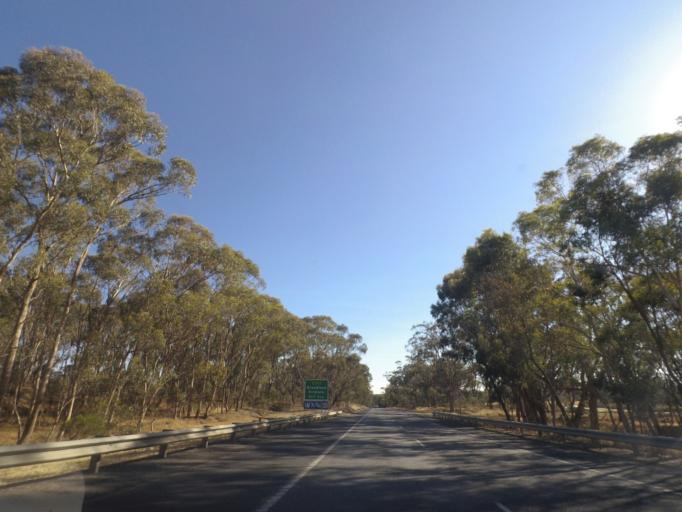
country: AU
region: Victoria
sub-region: Murrindindi
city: Kinglake West
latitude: -37.1737
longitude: 145.0743
